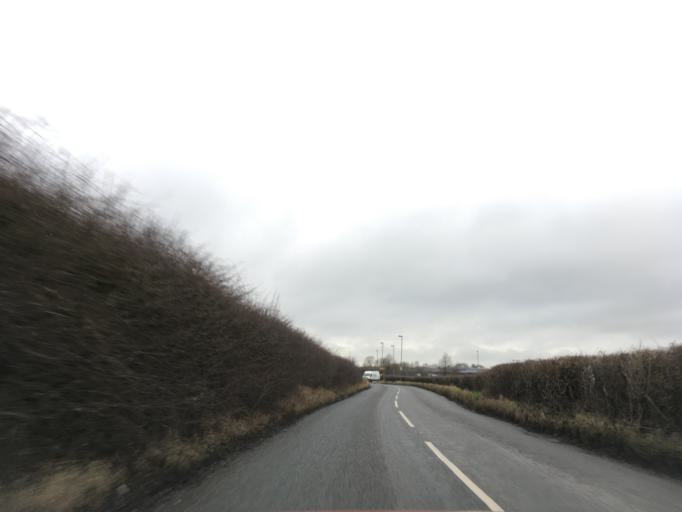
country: GB
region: England
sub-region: South Gloucestershire
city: Charfield
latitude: 51.6308
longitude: -2.3792
